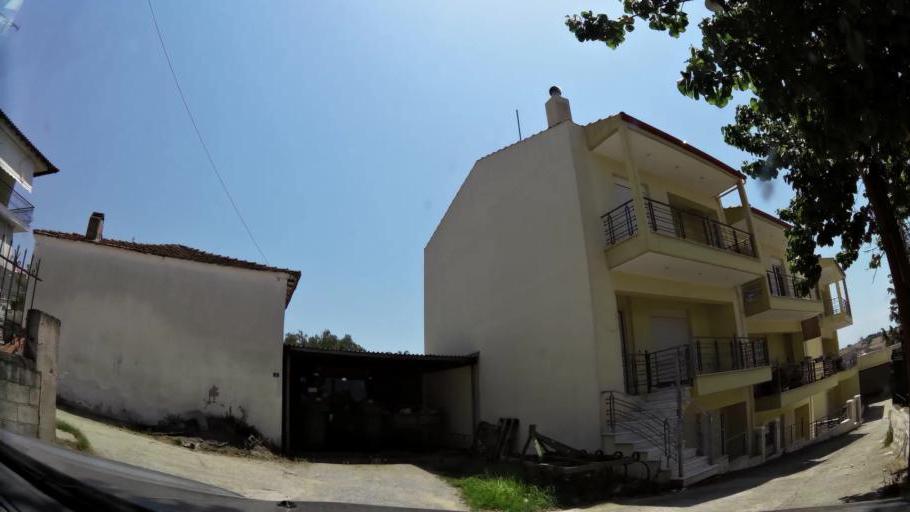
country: GR
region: Central Macedonia
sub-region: Nomos Thessalonikis
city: Trilofos
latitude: 40.4687
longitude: 22.9727
